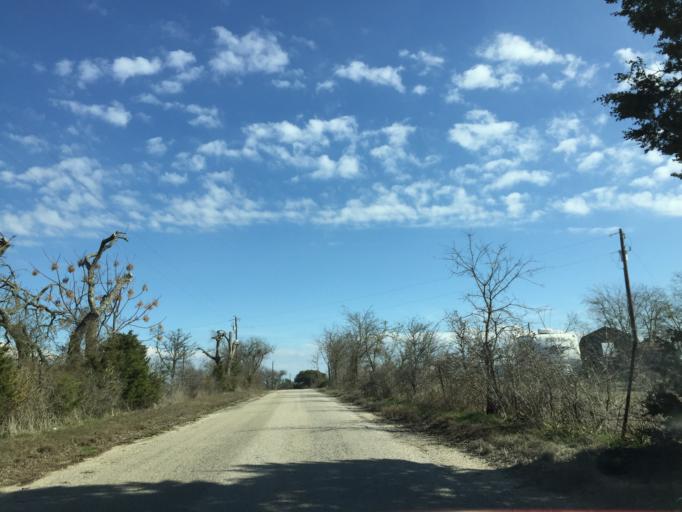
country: US
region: Texas
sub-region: Williamson County
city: Florence
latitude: 30.7828
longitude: -97.8957
